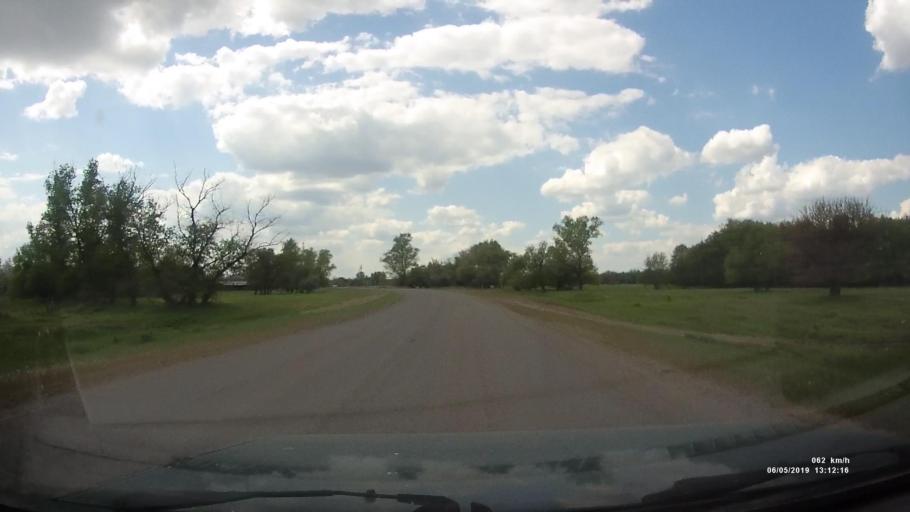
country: RU
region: Rostov
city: Ust'-Donetskiy
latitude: 47.7552
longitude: 40.9492
